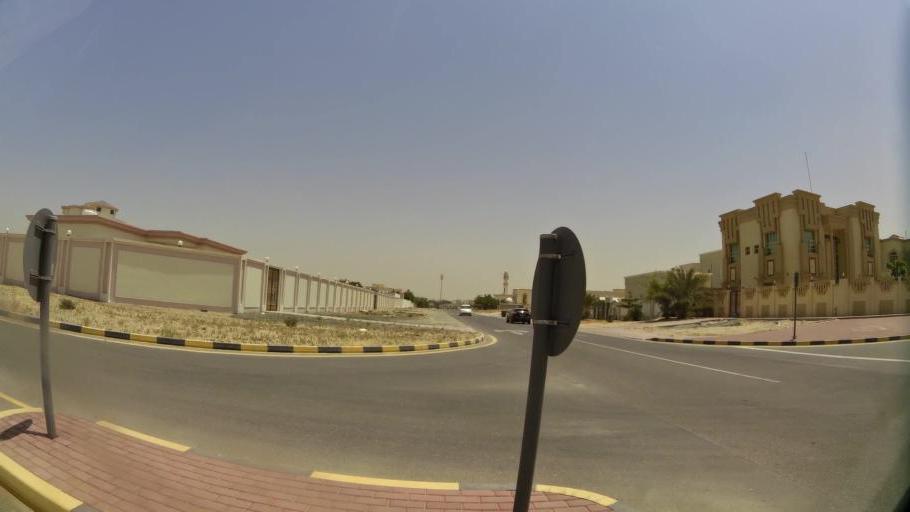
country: AE
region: Ajman
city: Ajman
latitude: 25.4057
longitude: 55.5220
